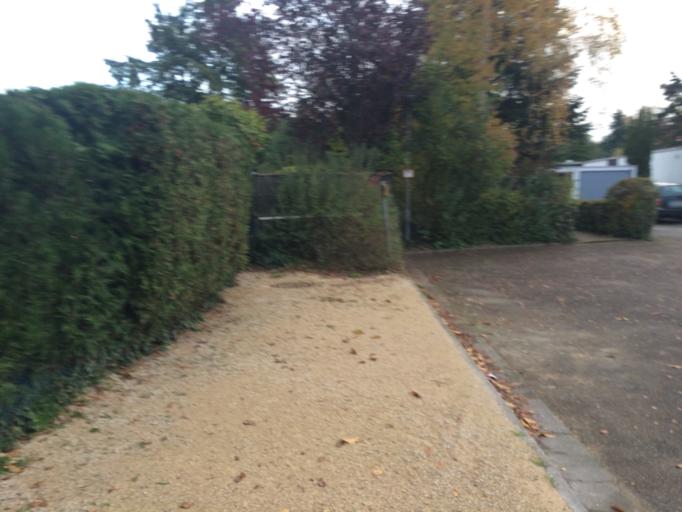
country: DE
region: Hesse
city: Morfelden-Walldorf
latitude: 50.0034
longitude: 8.5877
